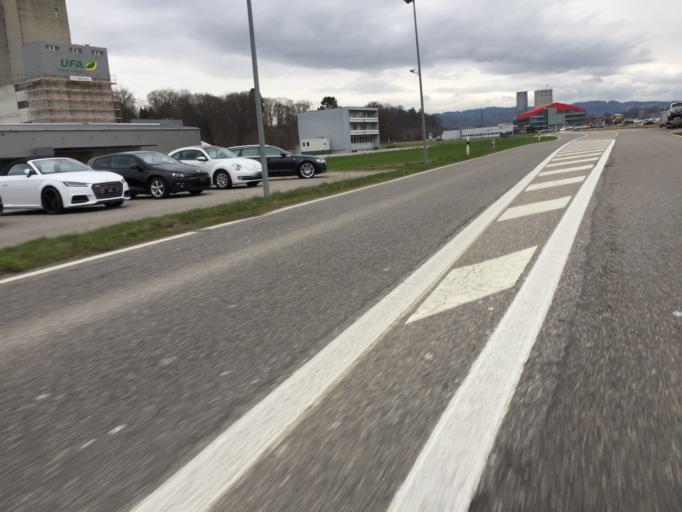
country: CH
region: Bern
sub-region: Emmental District
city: Lyssach
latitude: 47.0733
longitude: 7.5890
